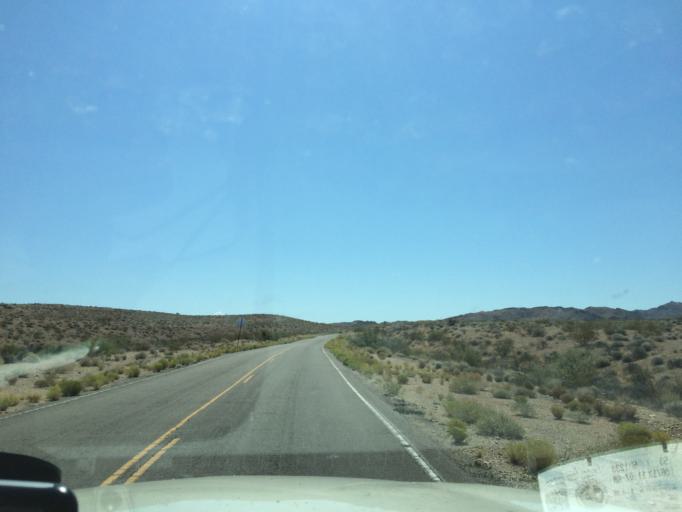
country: US
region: Nevada
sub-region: Clark County
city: Moapa Valley
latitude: 36.4433
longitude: -114.6525
